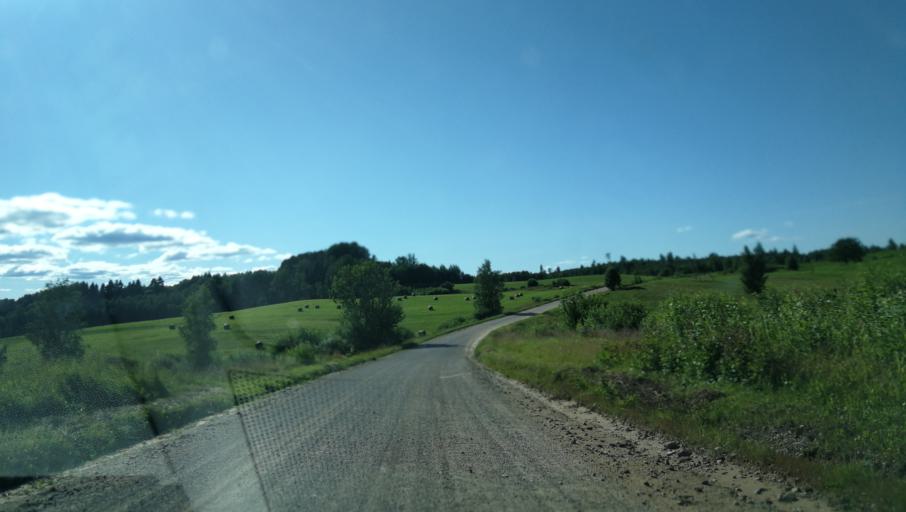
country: LV
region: Jaunpiebalga
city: Jaunpiebalga
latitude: 57.0165
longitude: 26.0439
